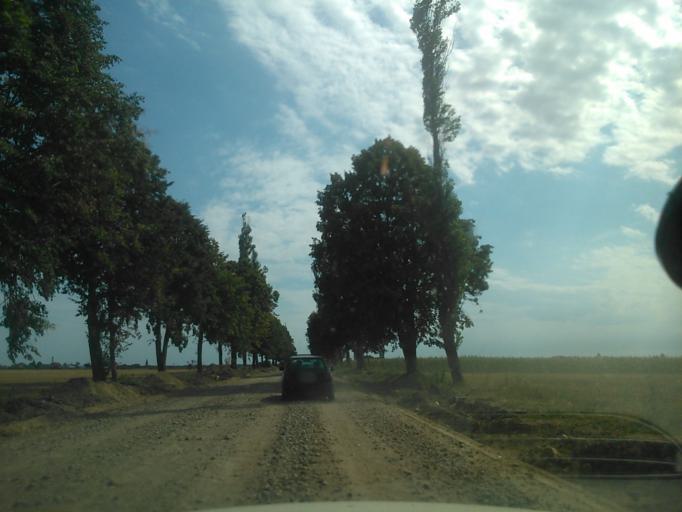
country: PL
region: Warmian-Masurian Voivodeship
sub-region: Powiat dzialdowski
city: Ilowo -Osada
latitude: 53.1841
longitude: 20.2879
